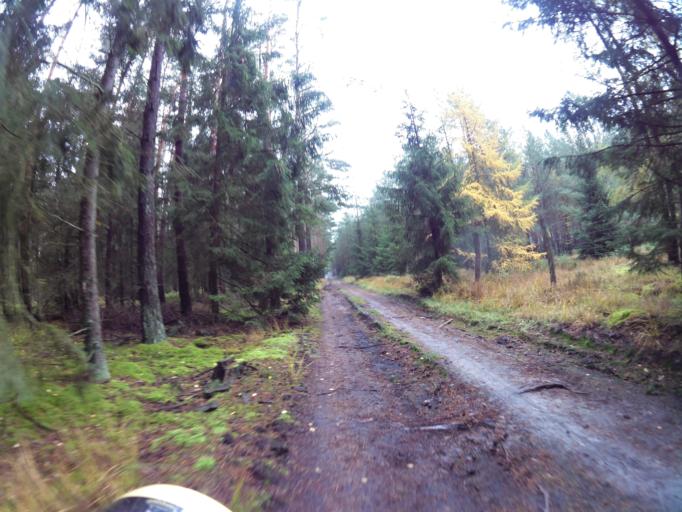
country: PL
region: West Pomeranian Voivodeship
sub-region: Powiat policki
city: Nowe Warpno
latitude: 53.6084
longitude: 14.3441
